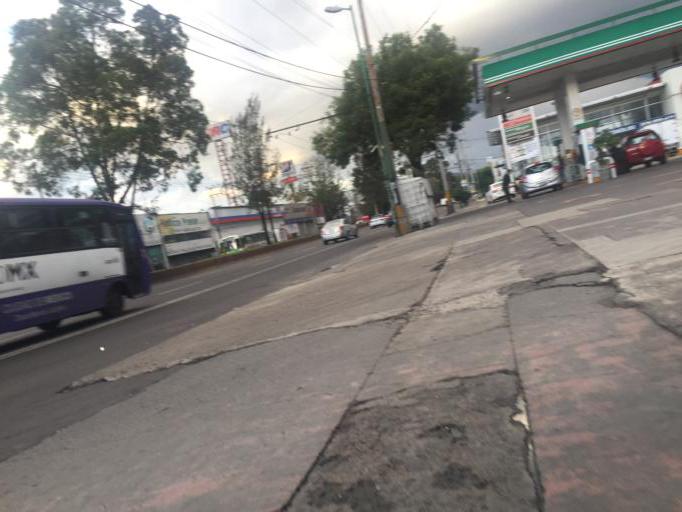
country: MX
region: Mexico City
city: Iztapalapa
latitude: 19.3545
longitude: -99.0829
